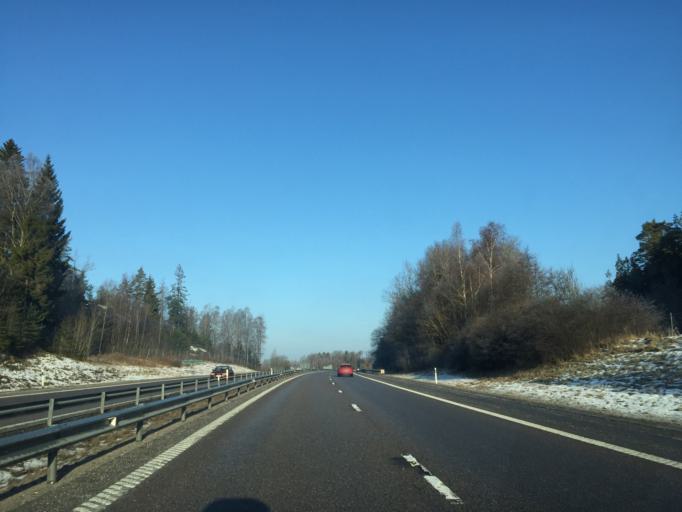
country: SE
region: Vaestra Goetaland
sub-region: Uddevalla Kommun
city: Ljungskile
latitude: 58.2953
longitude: 11.8638
